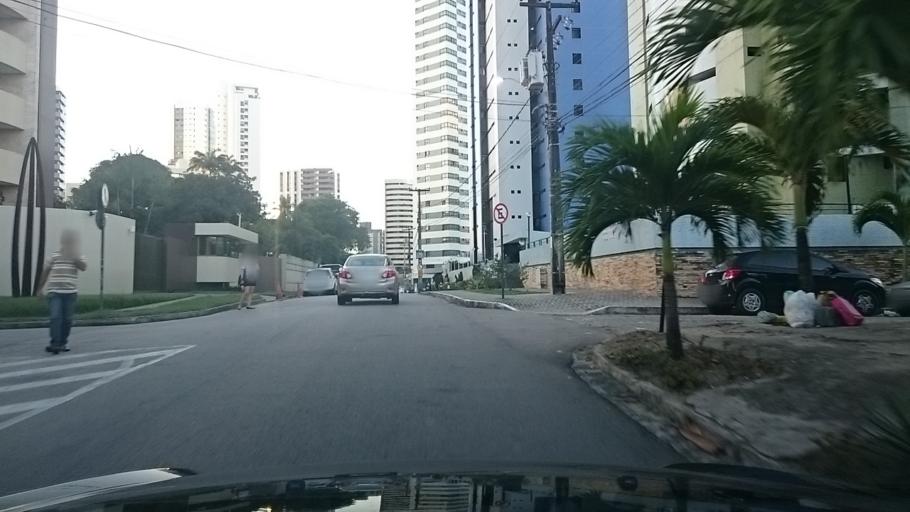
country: BR
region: Paraiba
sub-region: Joao Pessoa
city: Joao Pessoa
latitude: -7.1186
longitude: -34.8361
